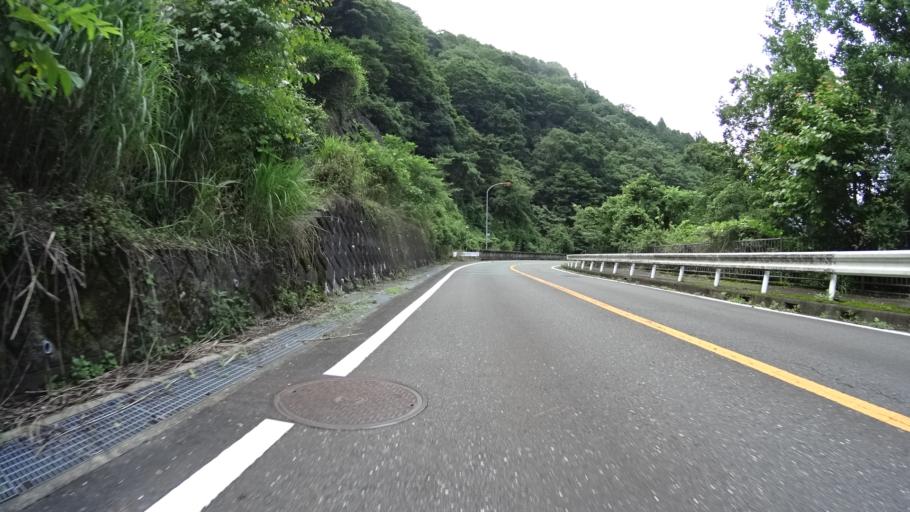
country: JP
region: Kanagawa
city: Hadano
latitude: 35.5045
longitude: 139.2294
